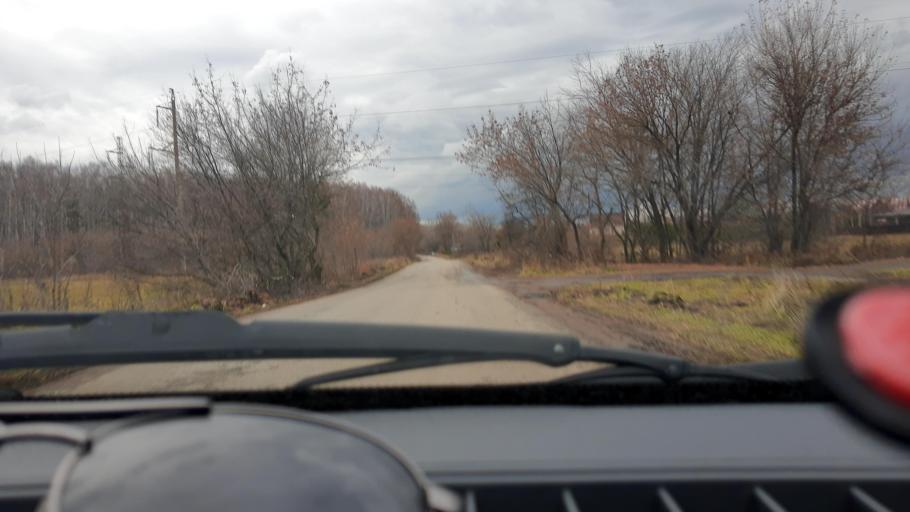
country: RU
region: Bashkortostan
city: Ufa
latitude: 54.7864
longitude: 56.1605
